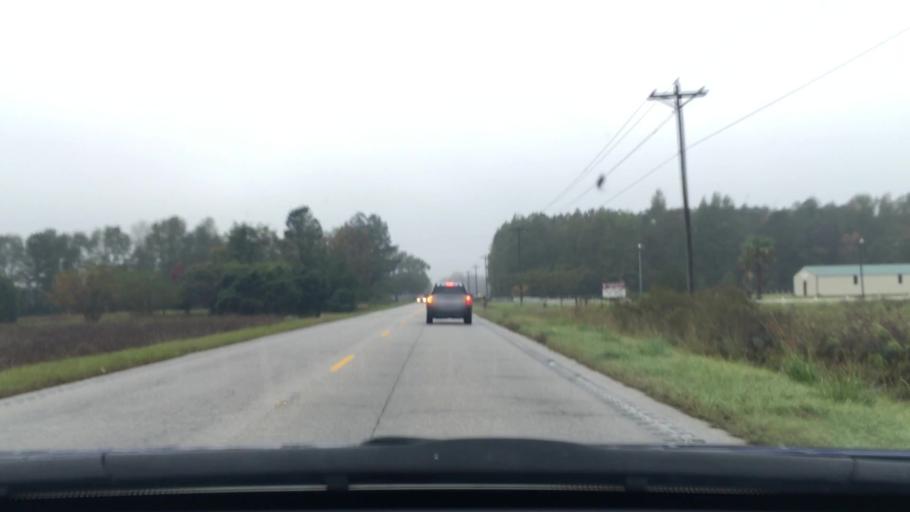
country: US
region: South Carolina
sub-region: Florence County
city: Timmonsville
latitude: 34.2245
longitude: -79.9998
